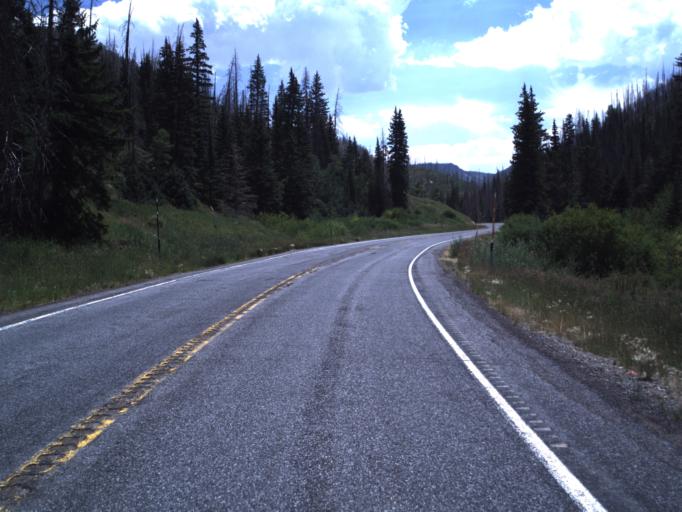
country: US
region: Utah
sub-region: Sanpete County
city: Fairview
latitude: 39.5798
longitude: -111.1863
